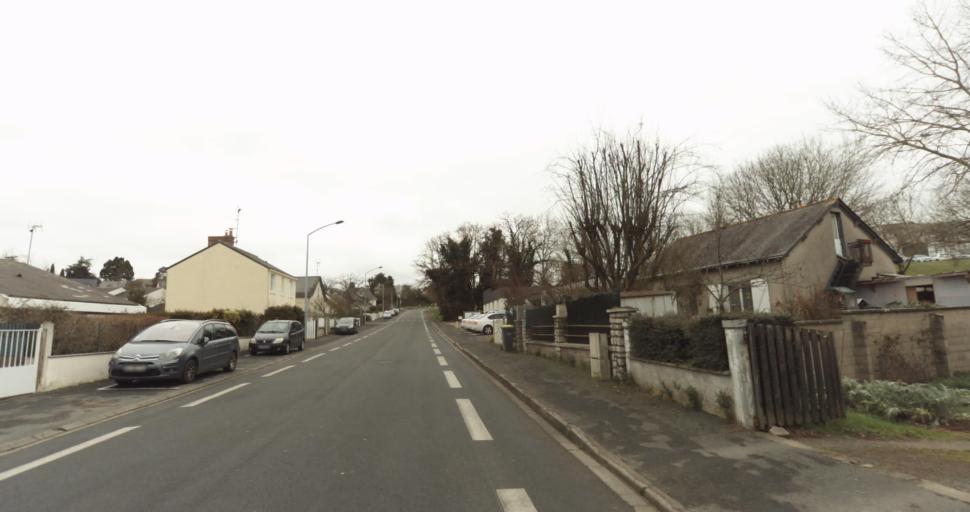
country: FR
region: Pays de la Loire
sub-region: Departement de Maine-et-Loire
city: Varrains
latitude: 47.2475
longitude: -0.0625
